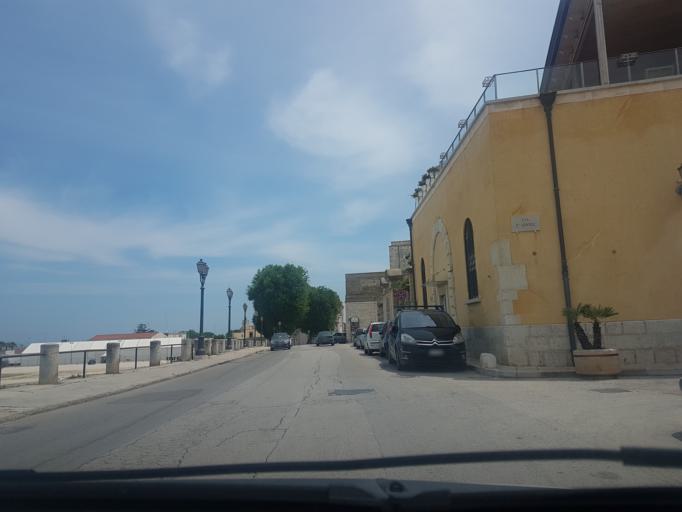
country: IT
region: Apulia
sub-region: Provincia di Barletta - Andria - Trani
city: Barletta
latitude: 41.3222
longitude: 16.2814
